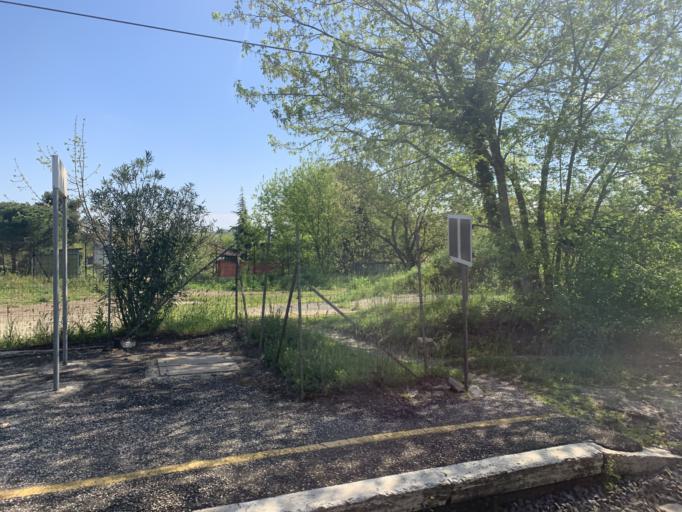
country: IT
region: Latium
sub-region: Citta metropolitana di Roma Capitale
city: Ciampino
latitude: 41.8301
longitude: 12.5693
